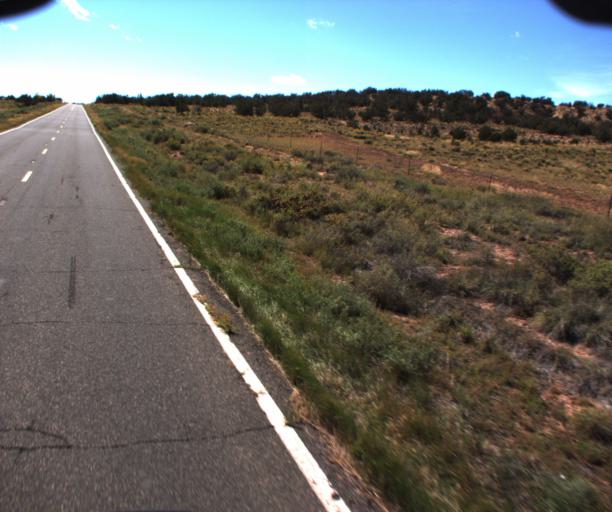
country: US
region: Arizona
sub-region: Apache County
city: Saint Johns
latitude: 34.7401
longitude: -109.2498
